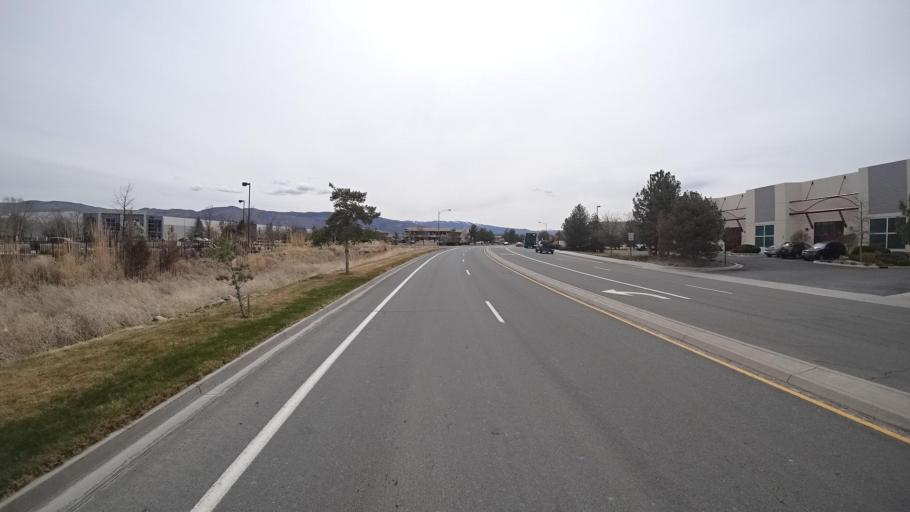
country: US
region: Nevada
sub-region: Washoe County
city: Sparks
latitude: 39.4493
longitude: -119.7494
